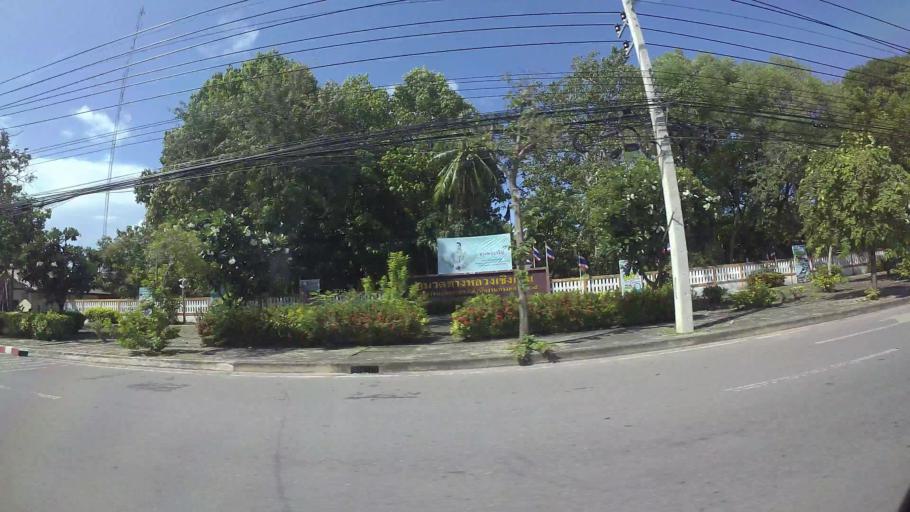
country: TH
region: Rayong
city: Rayong
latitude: 12.6756
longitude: 101.2890
